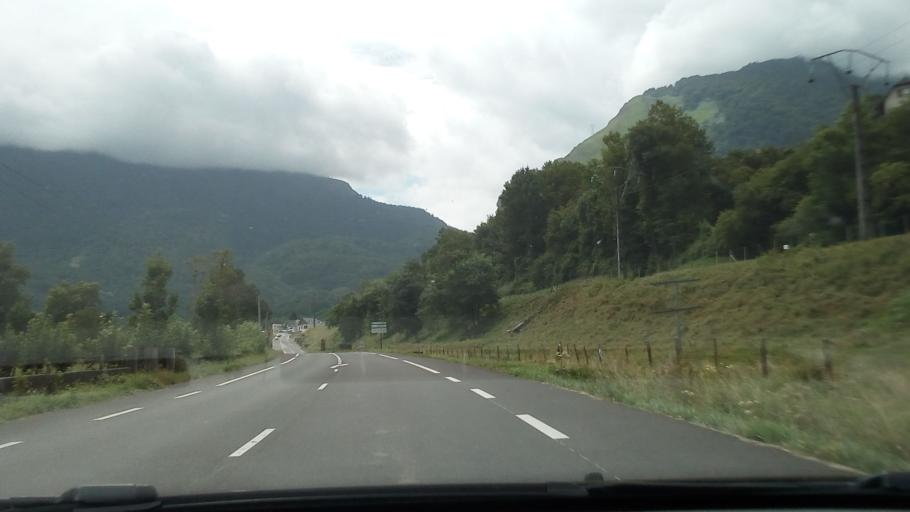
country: FR
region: Aquitaine
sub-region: Departement des Pyrenees-Atlantiques
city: Laruns
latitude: 42.9973
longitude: -0.4217
